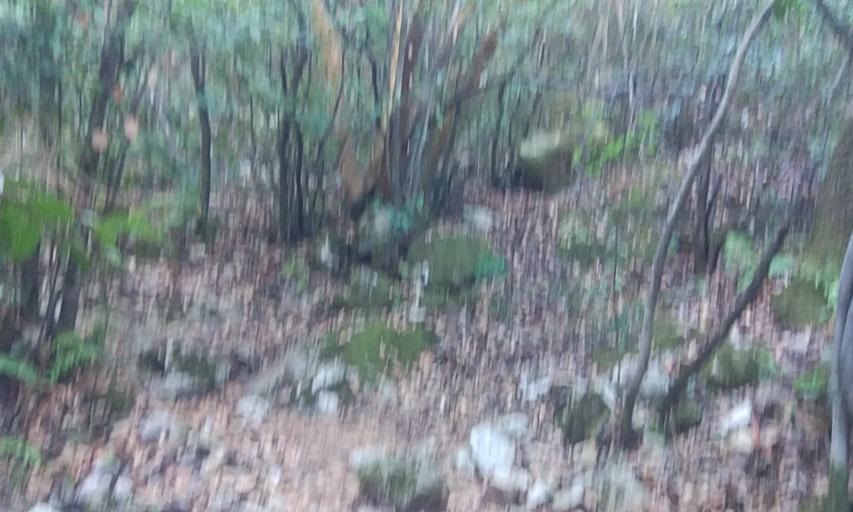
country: TR
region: Antalya
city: Tekirova
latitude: 36.3772
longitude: 30.4795
